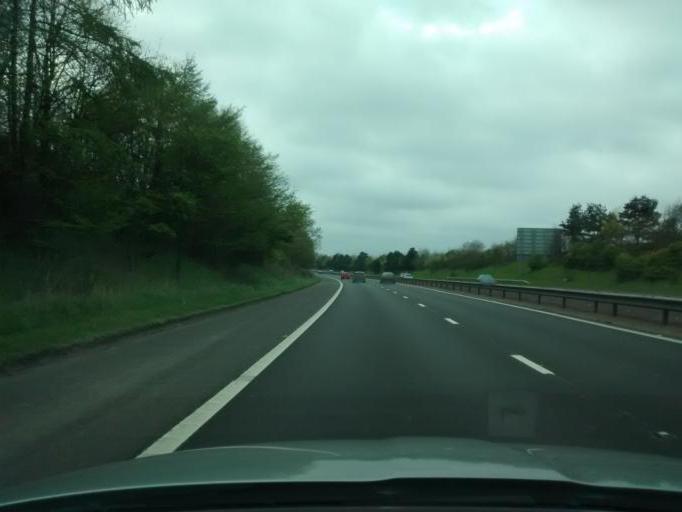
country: GB
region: Scotland
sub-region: West Lothian
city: Broxburn
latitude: 55.9269
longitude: -3.4399
